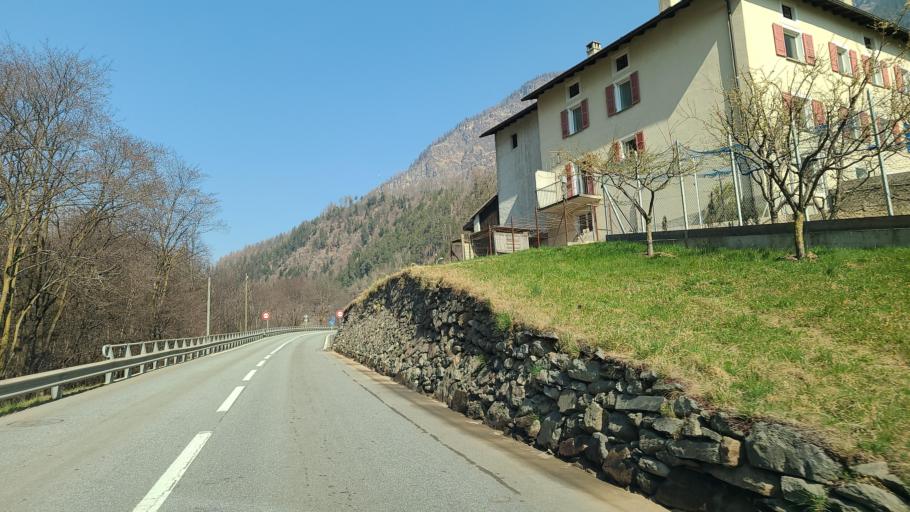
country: CH
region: Grisons
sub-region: Bernina District
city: Brusio
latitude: 46.2635
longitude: 10.1175
